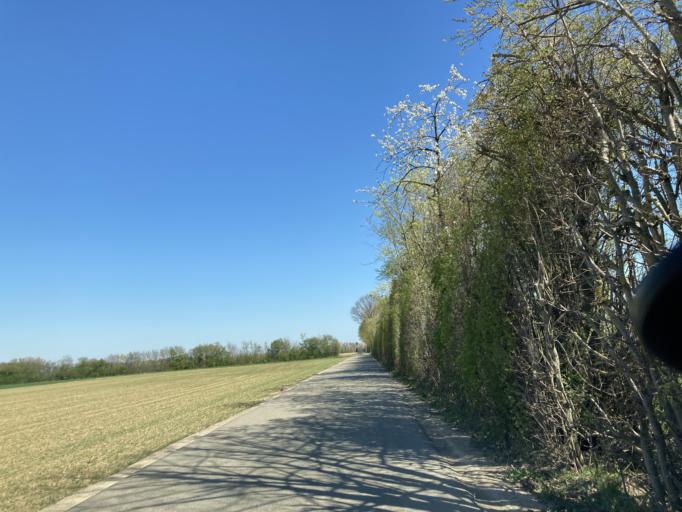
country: DE
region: Baden-Wuerttemberg
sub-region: Freiburg Region
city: Schliengen
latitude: 47.7731
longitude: 7.5592
